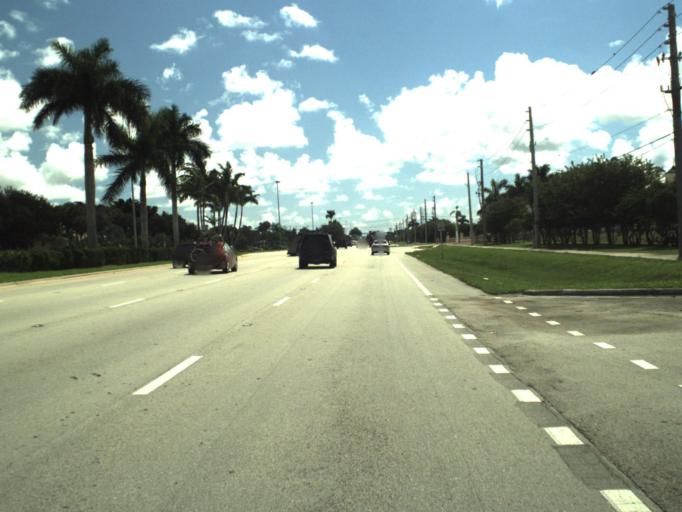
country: US
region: Florida
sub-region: Broward County
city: Cooper City
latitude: 26.0078
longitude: -80.2893
